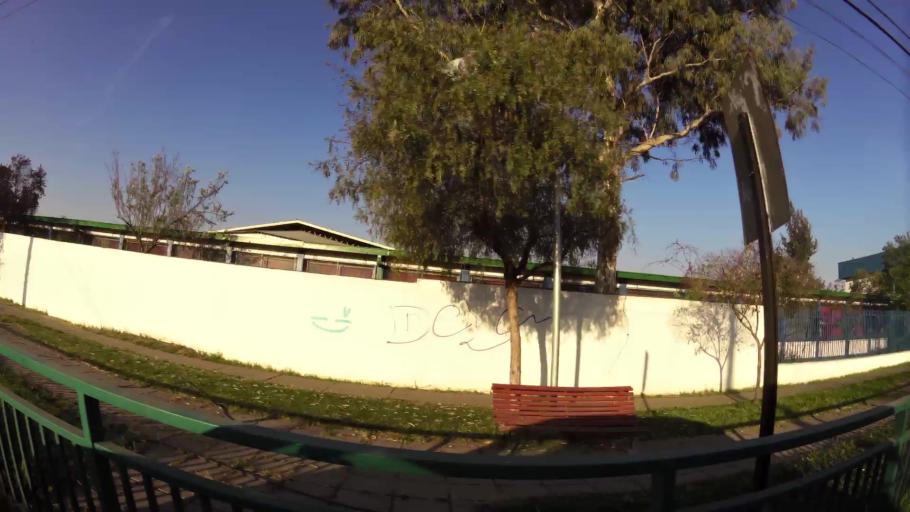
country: CL
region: Santiago Metropolitan
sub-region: Provincia de Santiago
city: La Pintana
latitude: -33.5307
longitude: -70.6234
